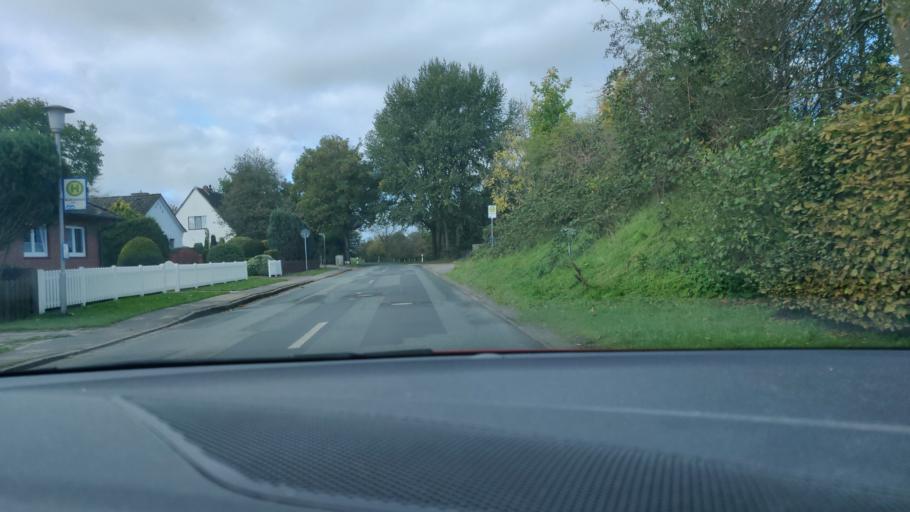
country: DE
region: Lower Saxony
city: Cuxhaven
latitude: 53.8318
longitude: 8.6670
